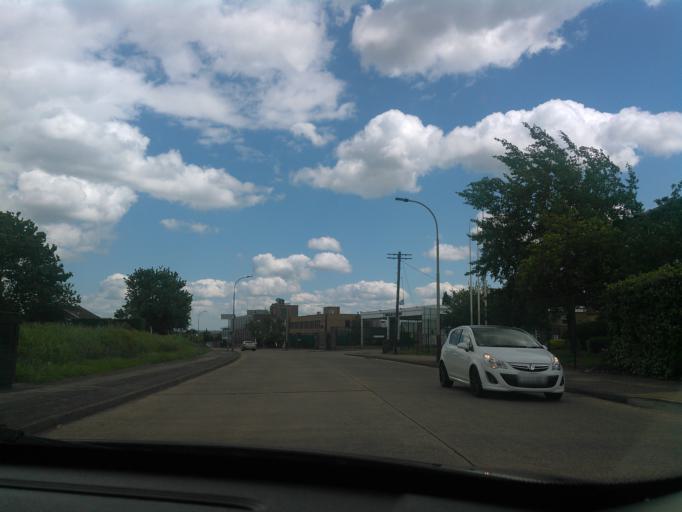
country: GB
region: England
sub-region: Leicestershire
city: Glenfield
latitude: 52.6335
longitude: -1.1972
